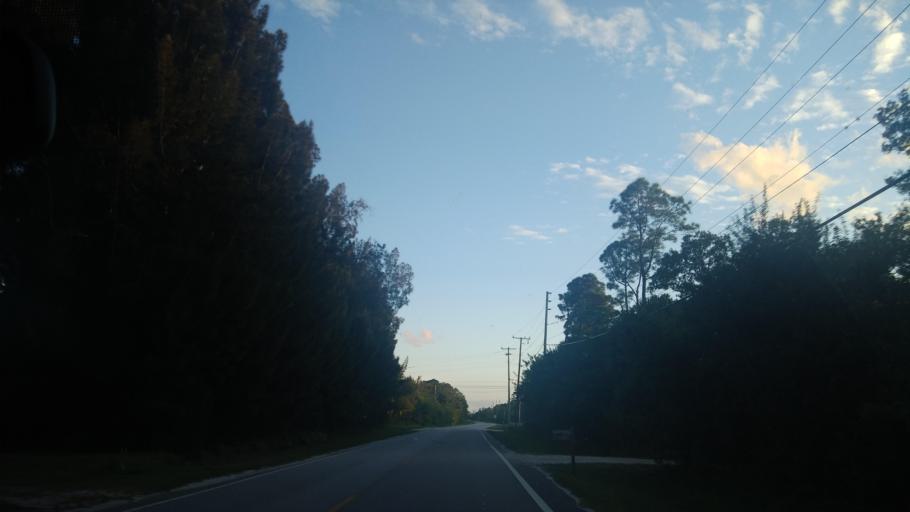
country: US
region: Florida
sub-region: Indian River County
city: Fellsmere
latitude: 27.7475
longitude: -80.5934
